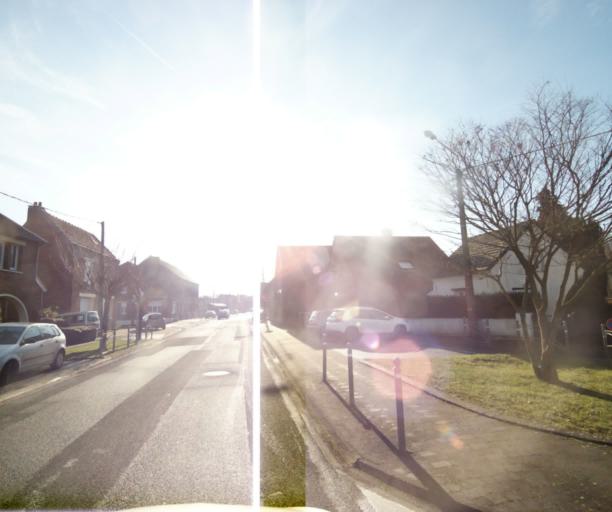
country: FR
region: Nord-Pas-de-Calais
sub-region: Departement du Nord
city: Maing
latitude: 50.3116
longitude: 3.4844
